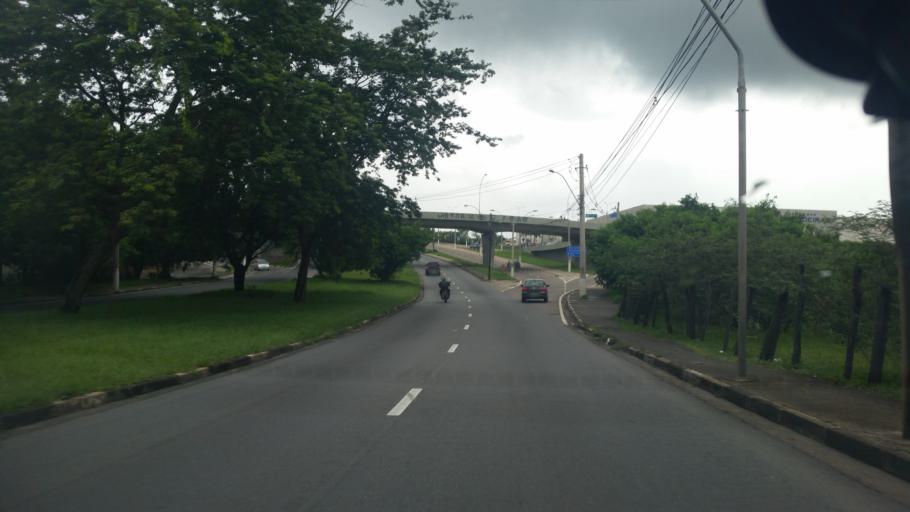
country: BR
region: Sao Paulo
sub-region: Campinas
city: Campinas
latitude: -22.9236
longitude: -47.1234
